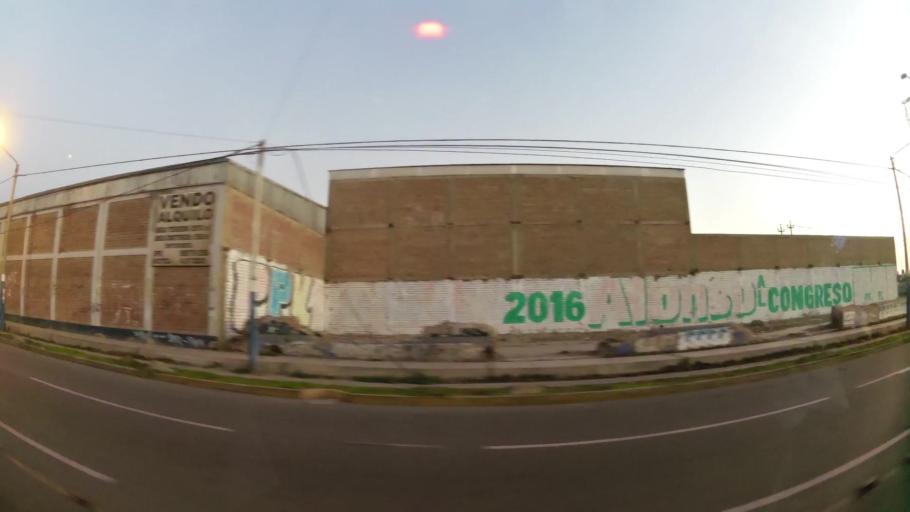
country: PE
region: Ica
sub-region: Provincia de Pisco
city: Pisco
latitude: -13.7097
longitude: -76.2112
